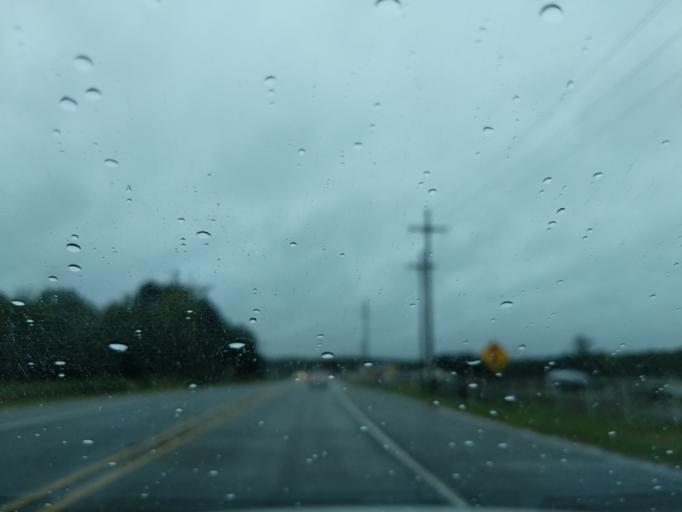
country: US
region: Louisiana
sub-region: Webster Parish
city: Minden
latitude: 32.6040
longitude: -93.2498
